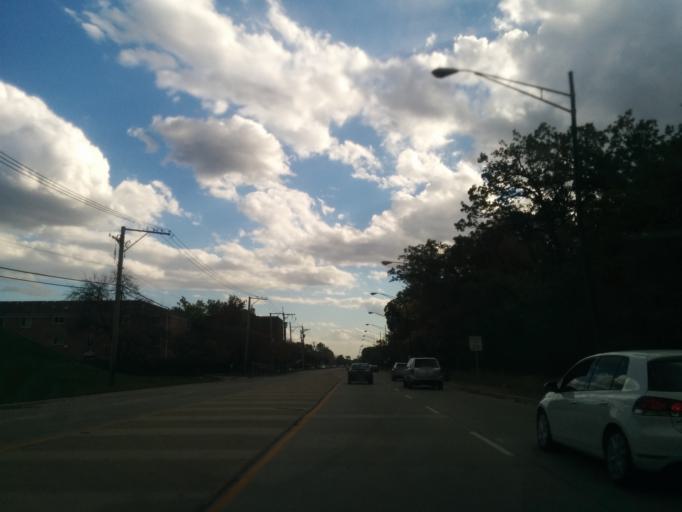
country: US
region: Illinois
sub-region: Cook County
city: Norridge
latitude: 41.9781
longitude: -87.8465
